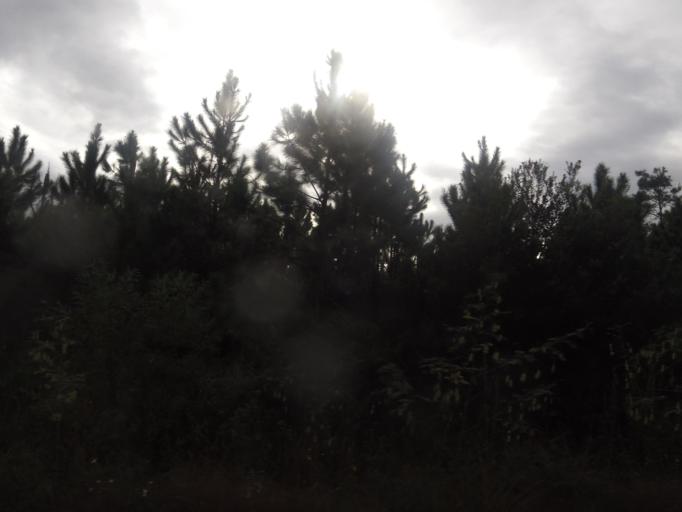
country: US
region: Florida
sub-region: Flagler County
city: Bunnell
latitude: 29.5587
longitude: -81.3319
